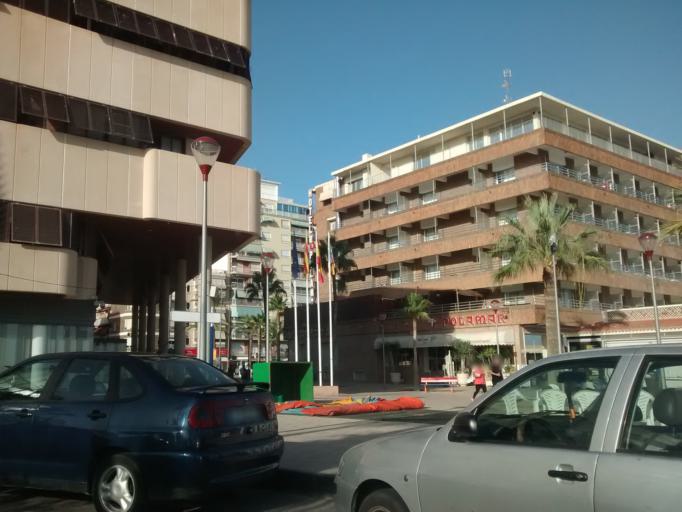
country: ES
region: Valencia
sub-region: Provincia de Alicante
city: Santa Pola
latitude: 38.1897
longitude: -0.5558
